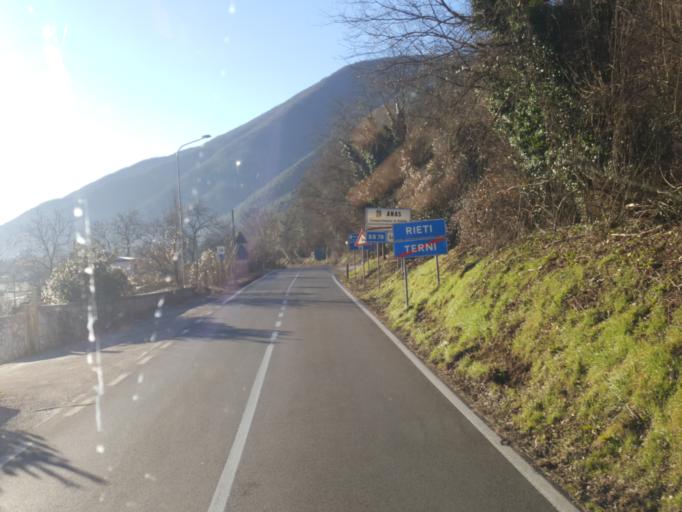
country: IT
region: Latium
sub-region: Provincia di Rieti
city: Colli sul Velino
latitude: 42.5105
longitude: 12.7395
